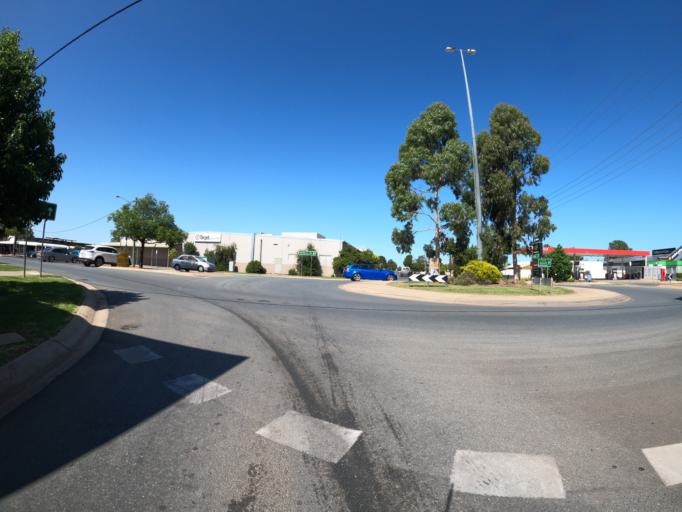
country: AU
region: Victoria
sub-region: Moira
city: Yarrawonga
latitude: -36.0149
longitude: 146.0043
